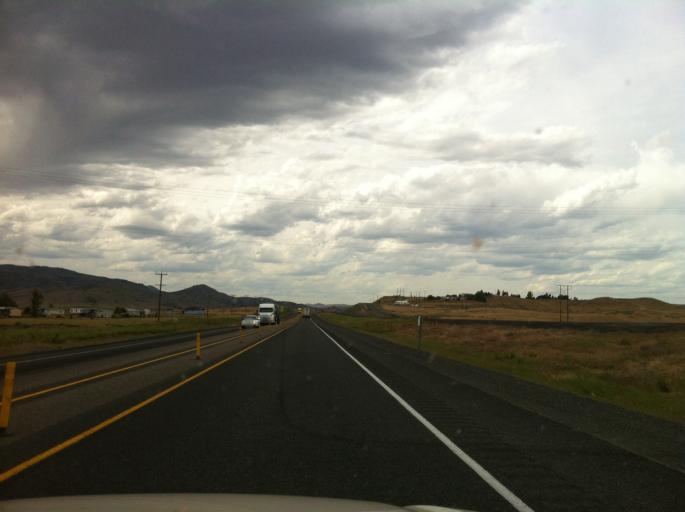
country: US
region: Oregon
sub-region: Baker County
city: Baker City
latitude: 44.5613
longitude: -117.4296
